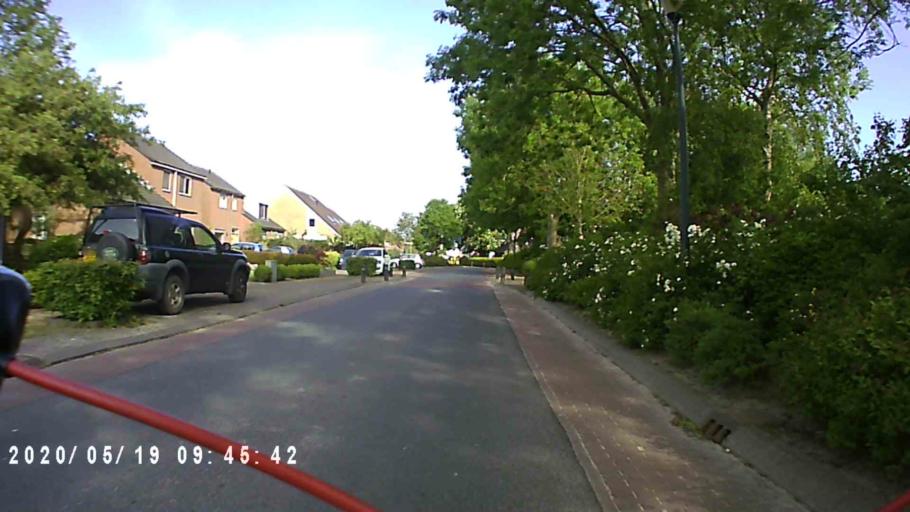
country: NL
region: Groningen
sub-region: Gemeente Zuidhorn
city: Grijpskerk
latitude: 53.2801
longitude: 6.2703
